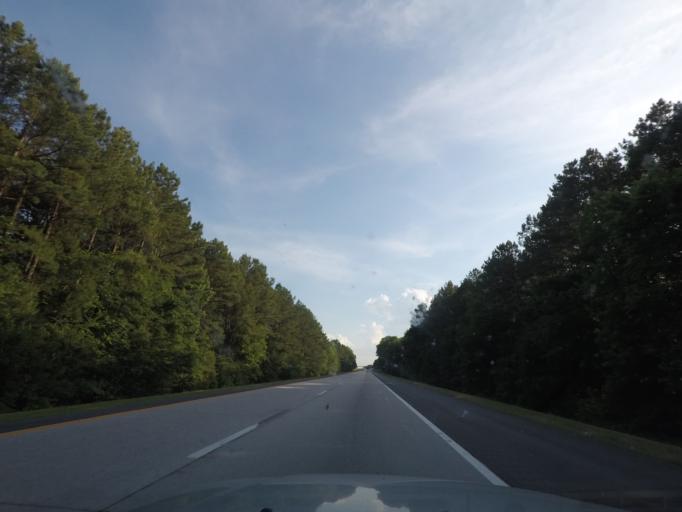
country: US
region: North Carolina
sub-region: Granville County
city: Creedmoor
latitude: 36.1573
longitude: -78.7166
